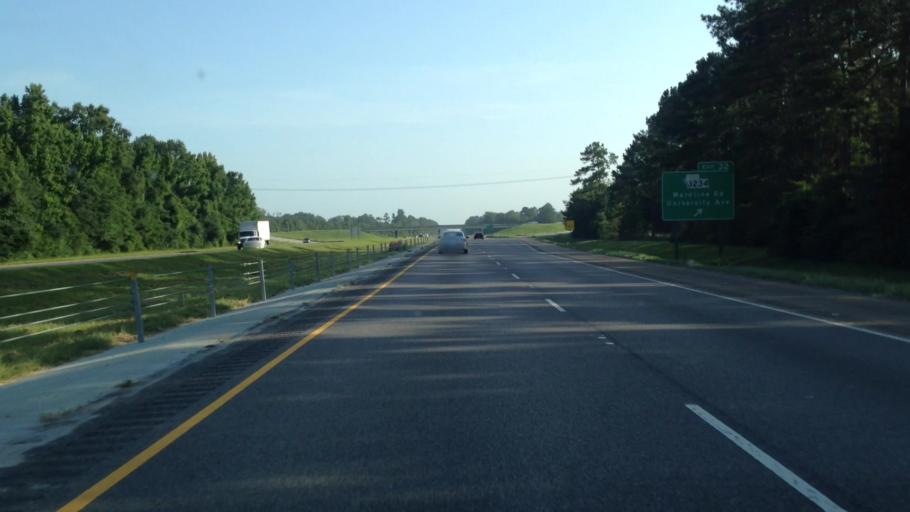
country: US
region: Louisiana
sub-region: Tangipahoa Parish
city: Natalbany
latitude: 30.5135
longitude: -90.5036
